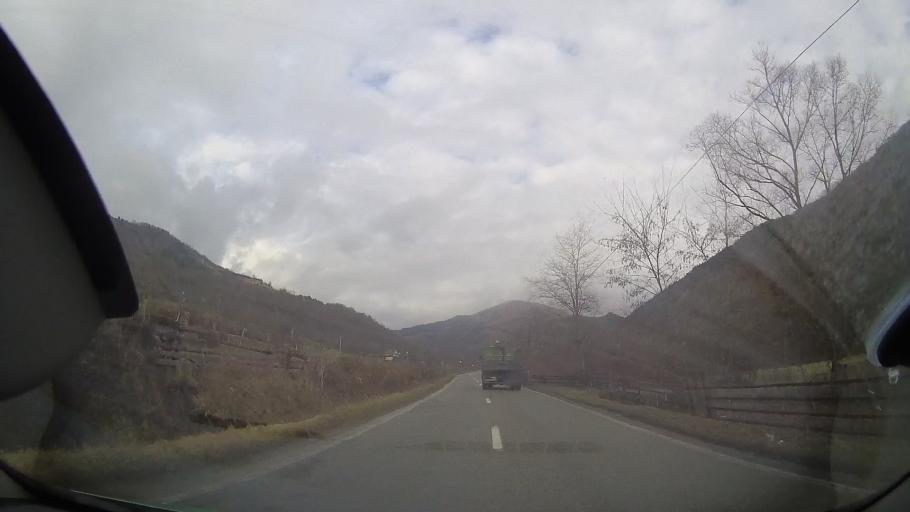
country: RO
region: Alba
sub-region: Comuna Ocolis
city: Ocolis
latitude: 46.4569
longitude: 23.4693
